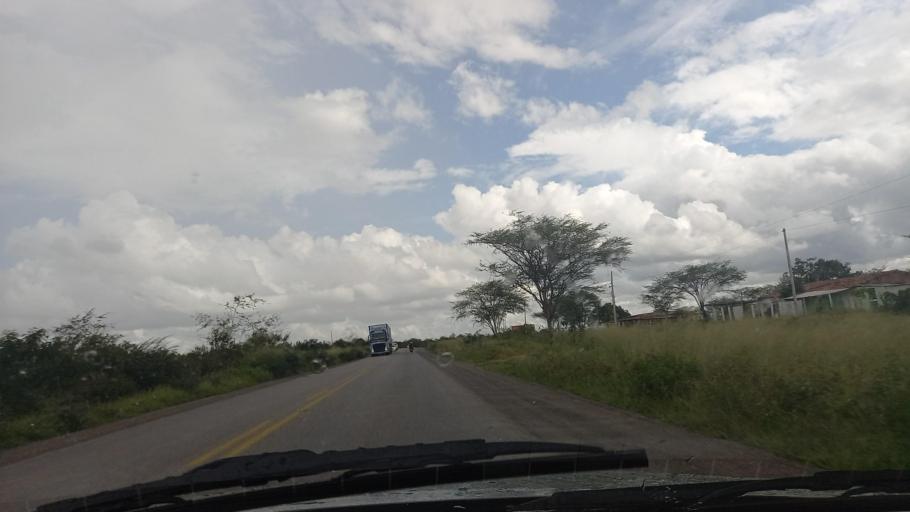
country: BR
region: Pernambuco
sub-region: Cachoeirinha
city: Cachoeirinha
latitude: -8.5601
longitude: -36.2762
